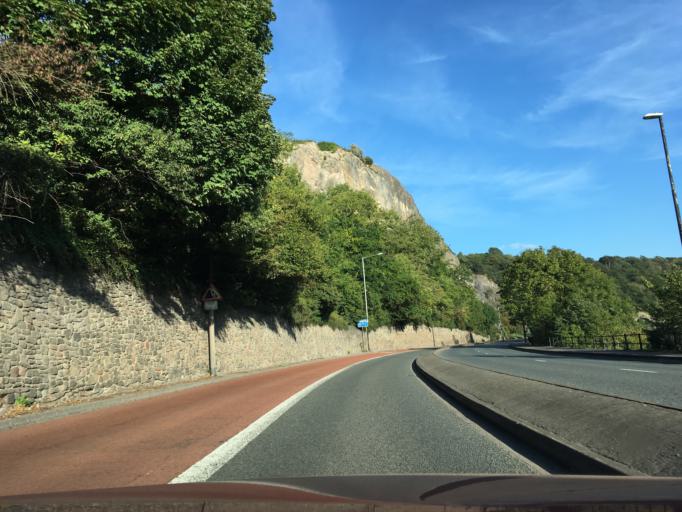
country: GB
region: England
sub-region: Bristol
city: Bristol
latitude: 51.4700
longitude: -2.6382
